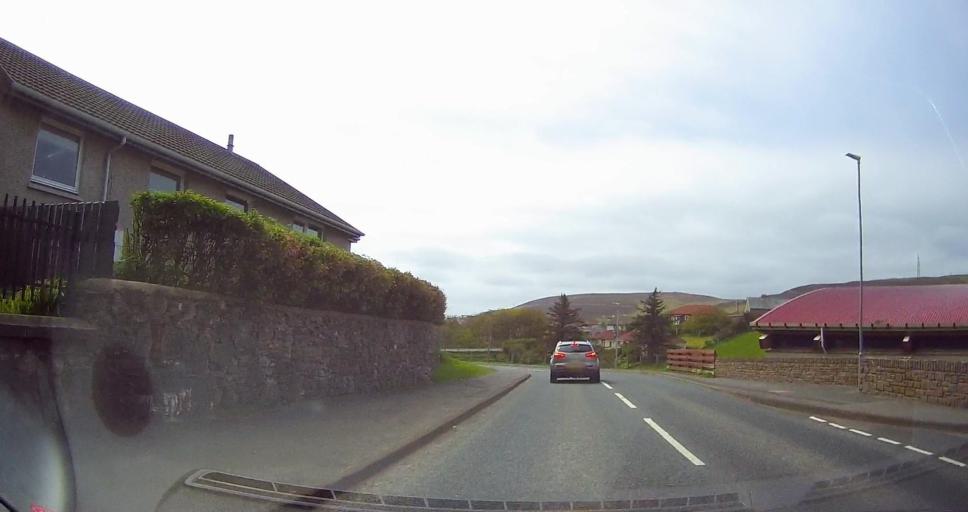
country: GB
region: Scotland
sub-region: Shetland Islands
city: Lerwick
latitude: 60.1398
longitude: -1.2723
